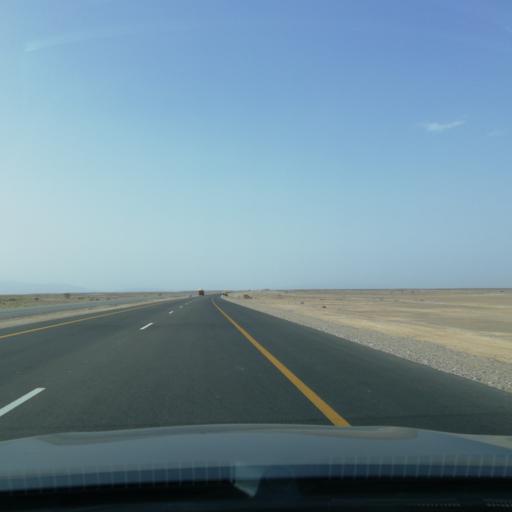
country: OM
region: Muhafazat ad Dakhiliyah
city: Adam
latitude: 22.1553
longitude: 57.5210
